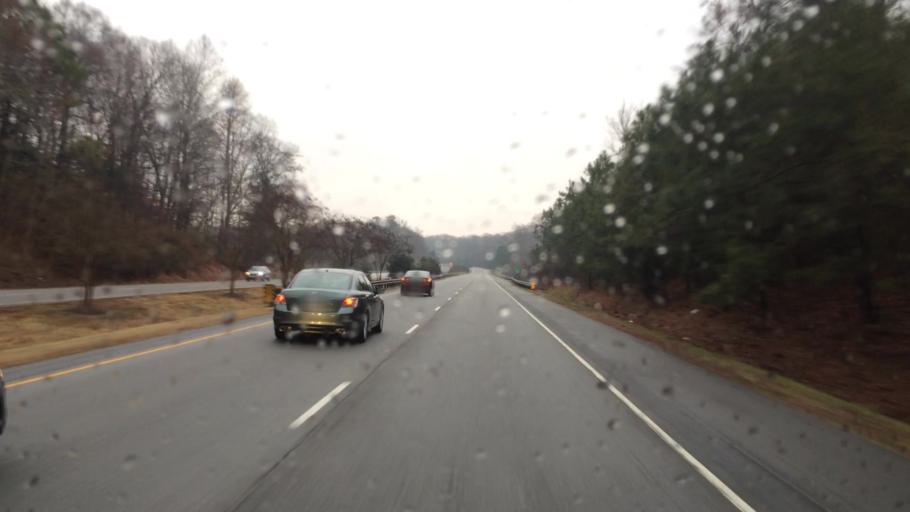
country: US
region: Virginia
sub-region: City of Williamsburg
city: Williamsburg
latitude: 37.2484
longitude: -76.7142
